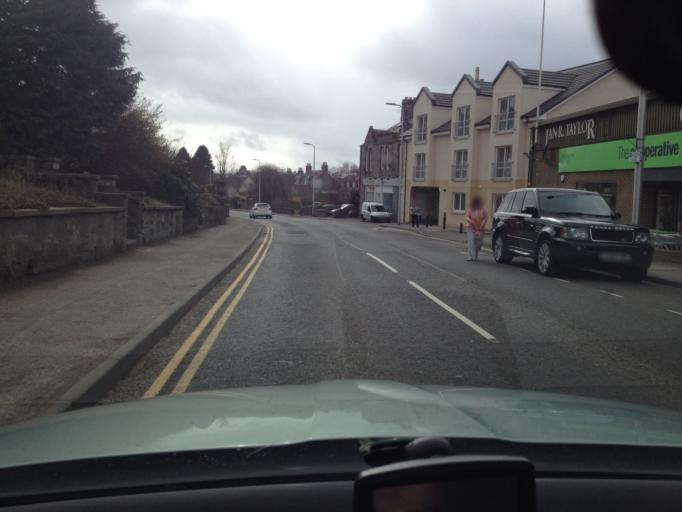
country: GB
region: Scotland
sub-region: Perth and Kinross
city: Scone
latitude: 56.4182
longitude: -3.4017
